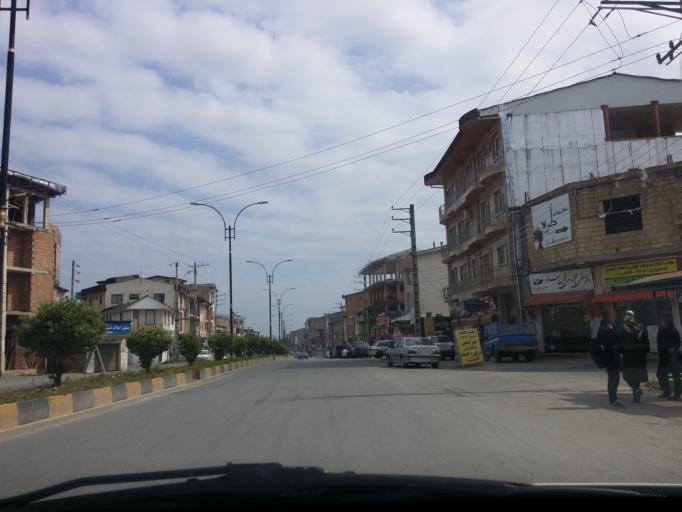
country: IR
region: Mazandaran
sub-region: Nowshahr
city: Nowshahr
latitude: 36.6310
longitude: 51.4858
